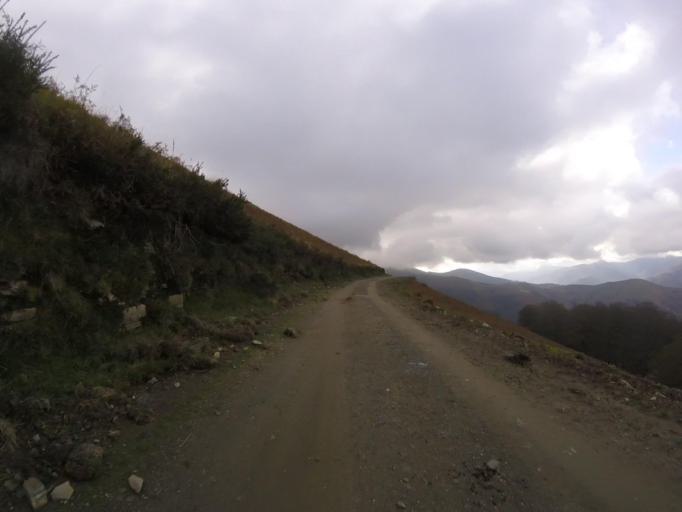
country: ES
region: Navarre
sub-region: Provincia de Navarra
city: Goizueta
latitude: 43.1975
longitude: -1.8234
